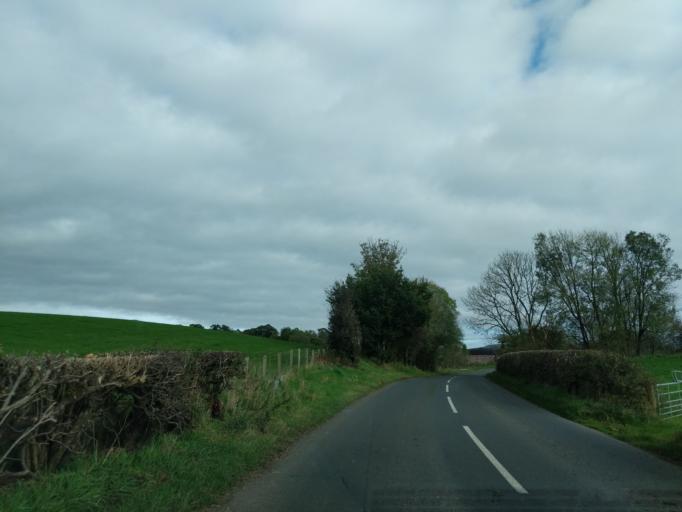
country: GB
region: Scotland
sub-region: Dumfries and Galloway
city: Thornhill
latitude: 55.2351
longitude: -3.8052
